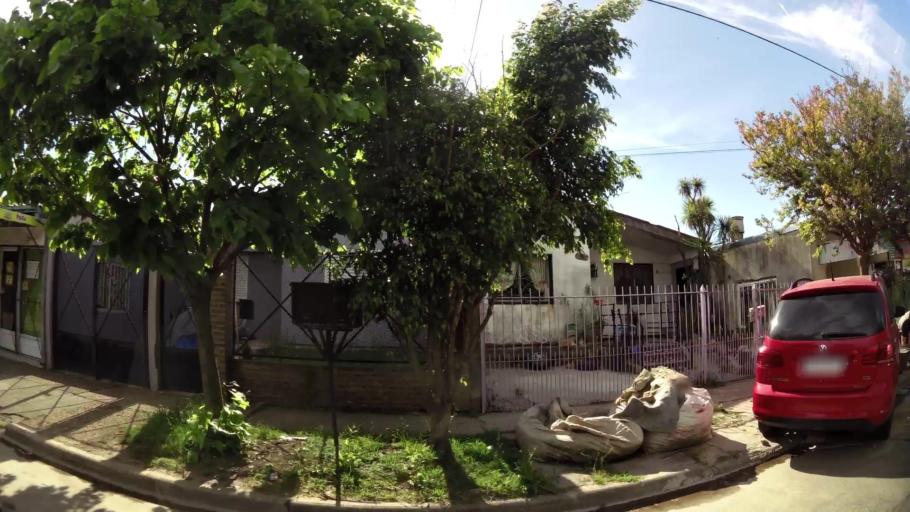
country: AR
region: Buenos Aires
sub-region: Partido de Almirante Brown
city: Adrogue
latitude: -34.8193
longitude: -58.3499
